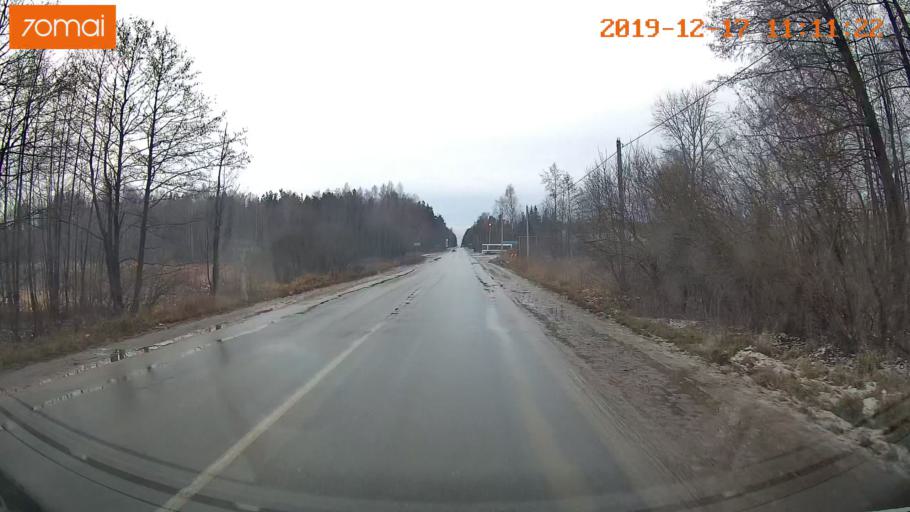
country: RU
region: Vladimir
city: Gus'-Khrustal'nyy
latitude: 55.5871
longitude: 40.6371
